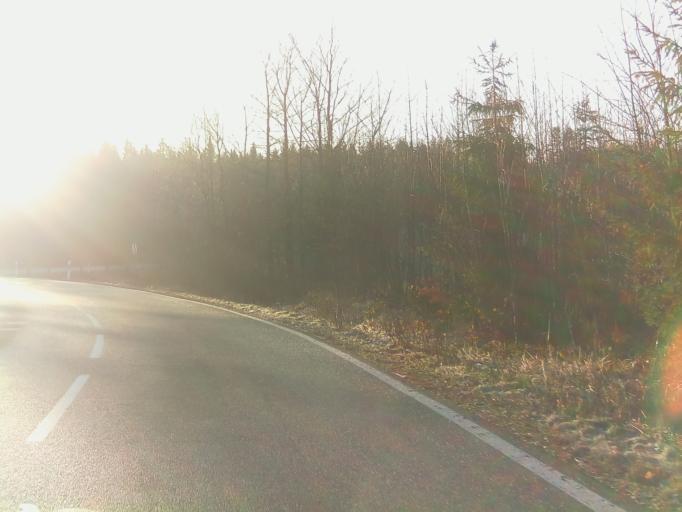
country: DE
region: Thuringia
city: Judenbach
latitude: 50.4176
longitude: 11.2298
